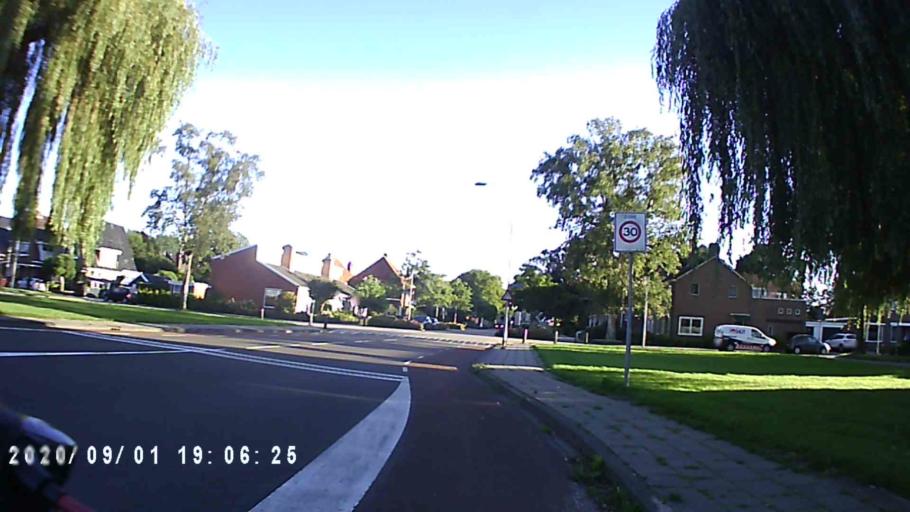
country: NL
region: Groningen
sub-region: Gemeente Veendam
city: Veendam
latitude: 53.1097
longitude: 6.8781
